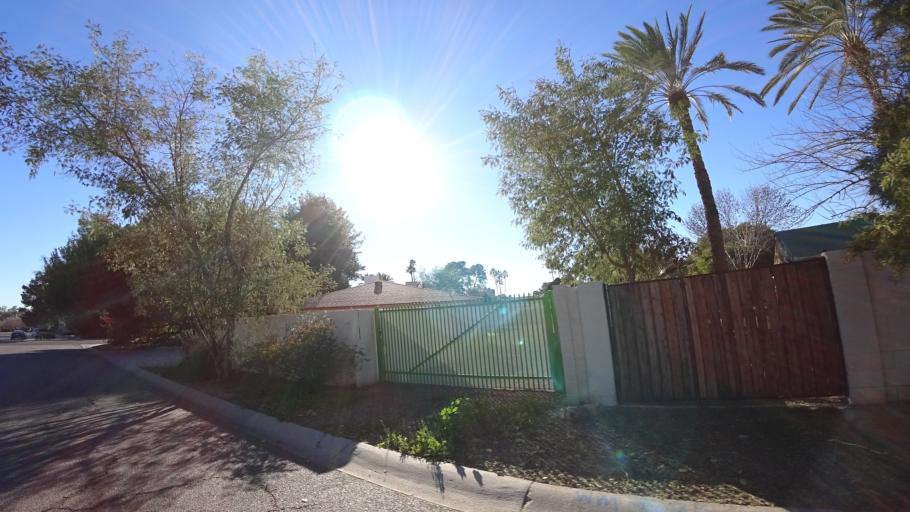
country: US
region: Arizona
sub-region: Maricopa County
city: Phoenix
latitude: 33.5170
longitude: -112.0520
